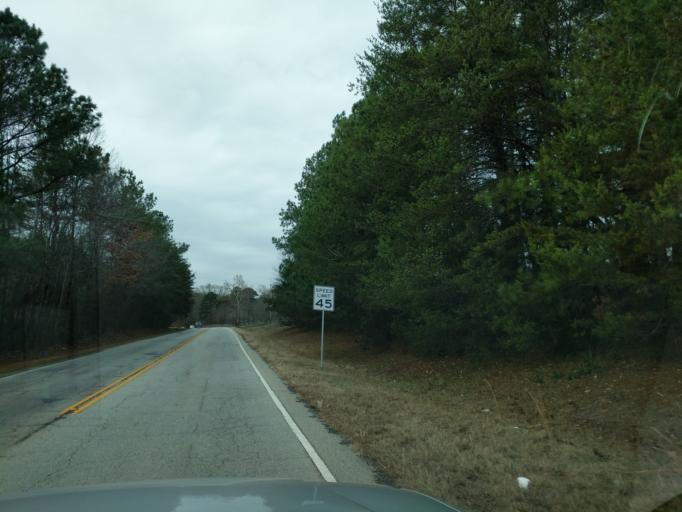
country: US
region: South Carolina
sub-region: Spartanburg County
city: Wellford
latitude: 34.8789
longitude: -82.0763
